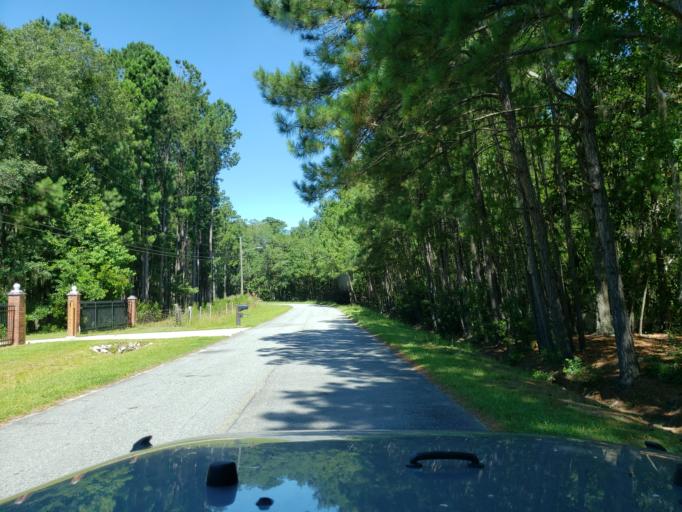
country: US
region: Georgia
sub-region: Chatham County
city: Georgetown
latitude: 31.9634
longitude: -81.2174
